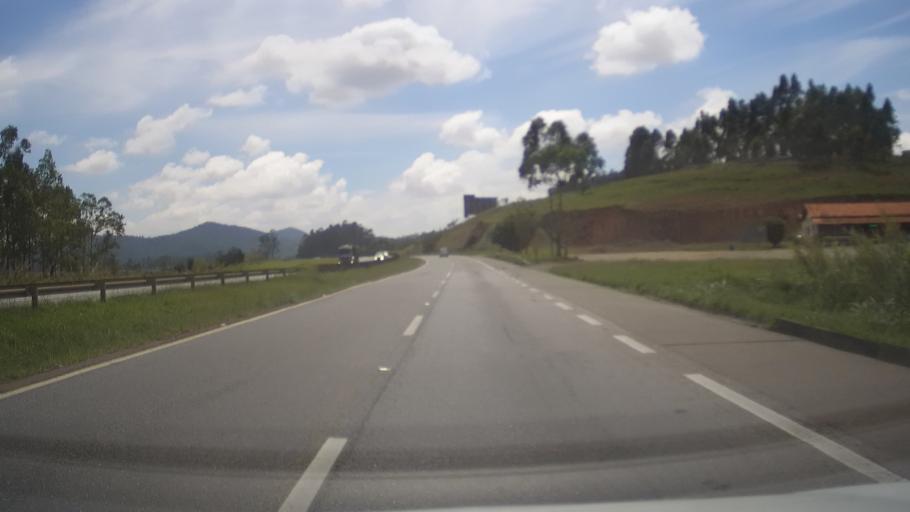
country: BR
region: Minas Gerais
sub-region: Santa Rita Do Sapucai
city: Santa Rita do Sapucai
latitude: -22.0945
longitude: -45.7119
